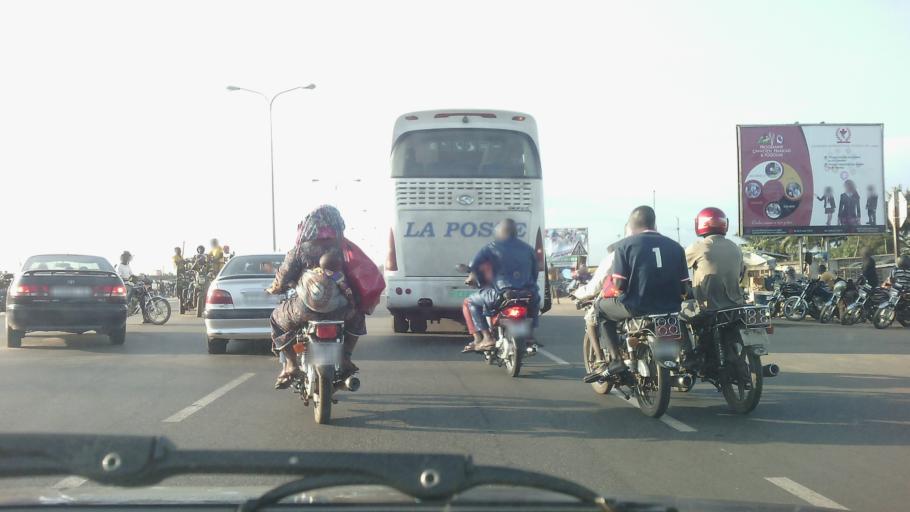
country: TG
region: Maritime
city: Lome
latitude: 6.2535
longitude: 1.2088
